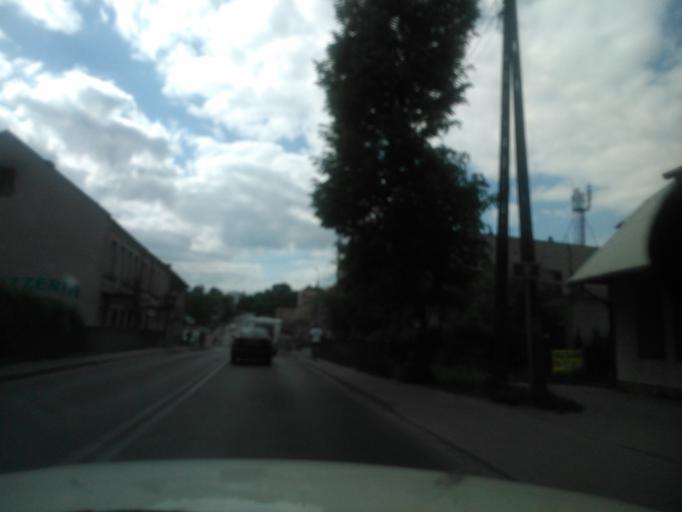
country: PL
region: Masovian Voivodeship
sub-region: Powiat radomski
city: Ilza
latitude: 51.1632
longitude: 21.2397
